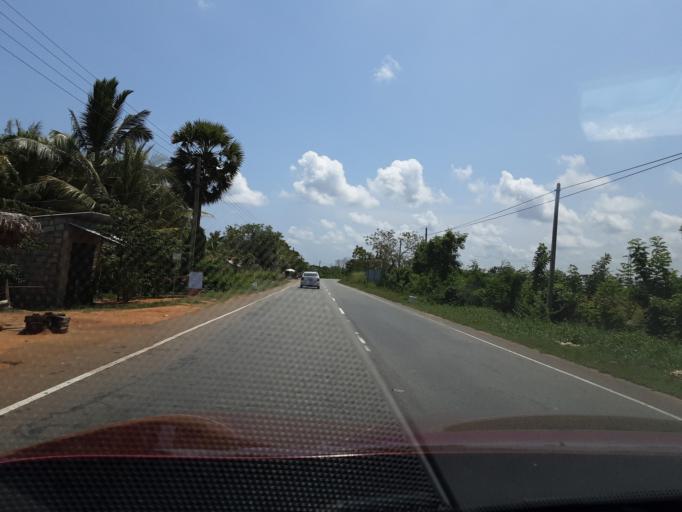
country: LK
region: Southern
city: Tangalla
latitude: 6.2167
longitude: 81.2111
